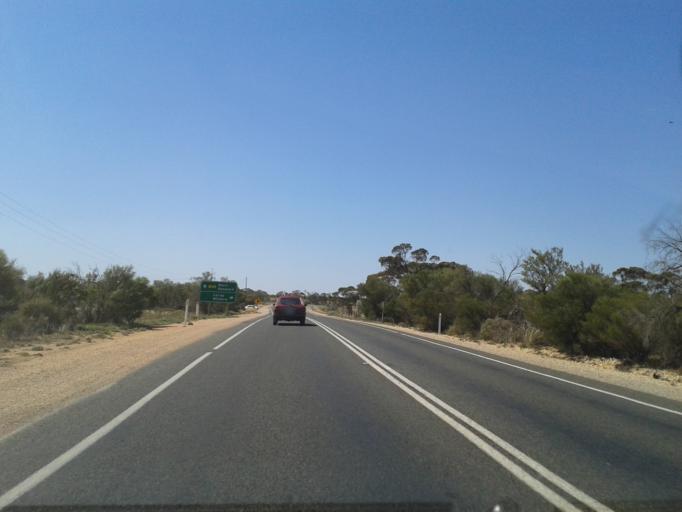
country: AU
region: South Australia
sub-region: Loxton Waikerie
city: Loxton
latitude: -34.3799
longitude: 140.6047
